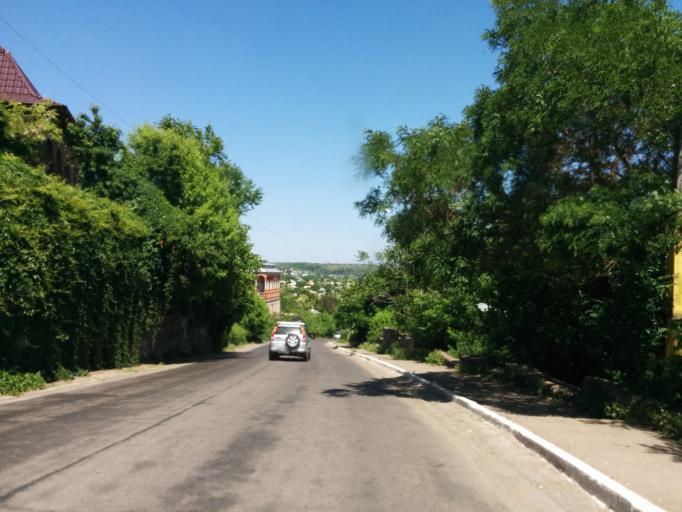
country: MD
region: Raionul Soroca
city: Soroca
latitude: 48.1605
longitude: 28.2963
